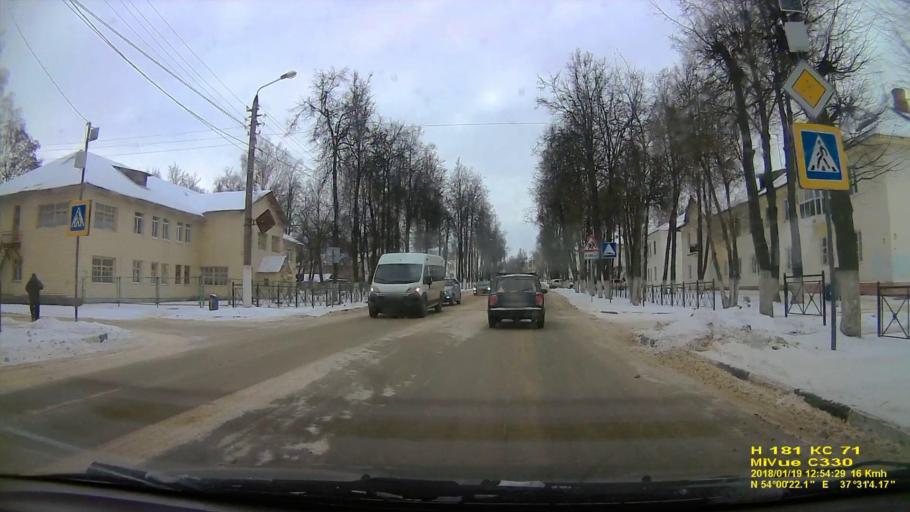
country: RU
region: Tula
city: Shchekino
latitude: 54.0061
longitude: 37.5178
